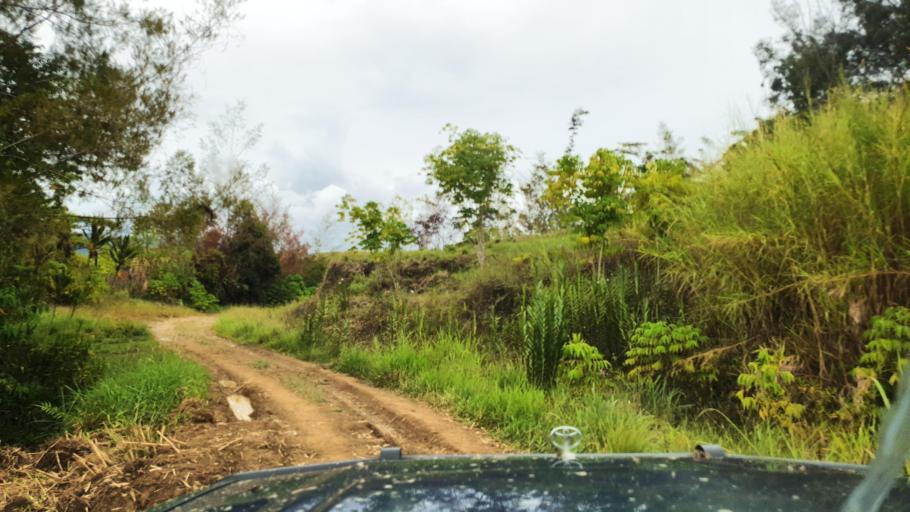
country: PG
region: Jiwaka
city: Minj
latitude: -5.9285
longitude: 144.7448
